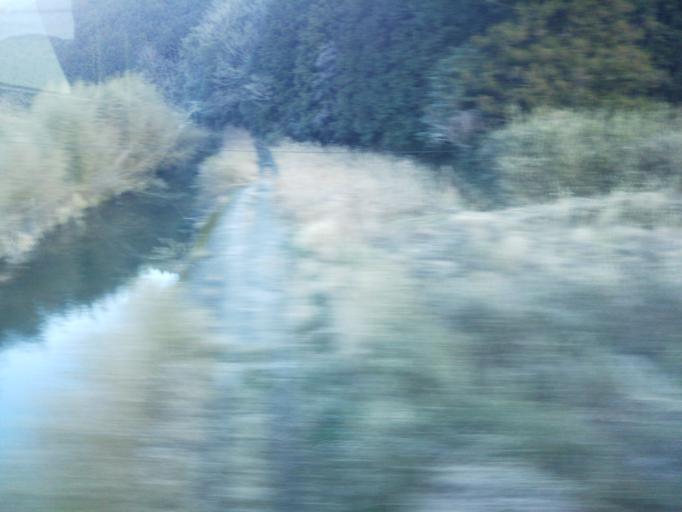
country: JP
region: Kochi
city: Susaki
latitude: 33.2733
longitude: 133.1713
